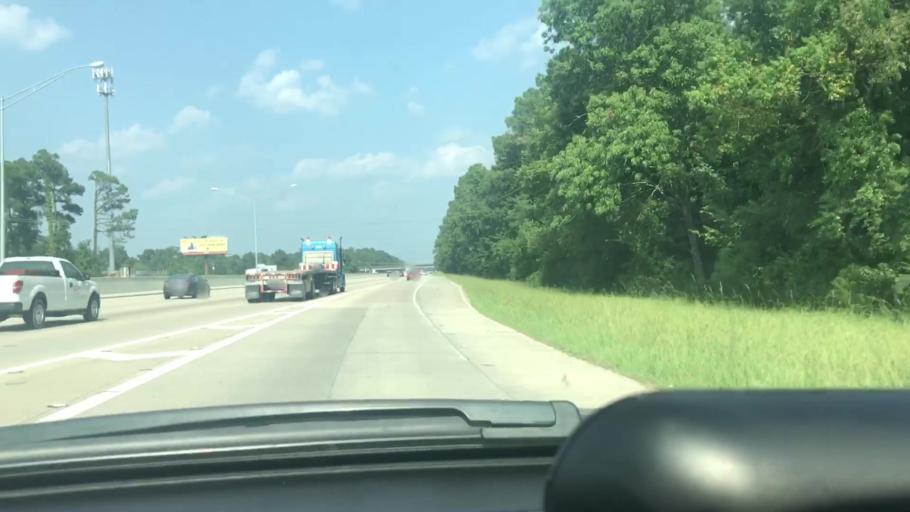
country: US
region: Louisiana
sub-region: Livingston Parish
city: Denham Springs
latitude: 30.4557
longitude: -90.9529
